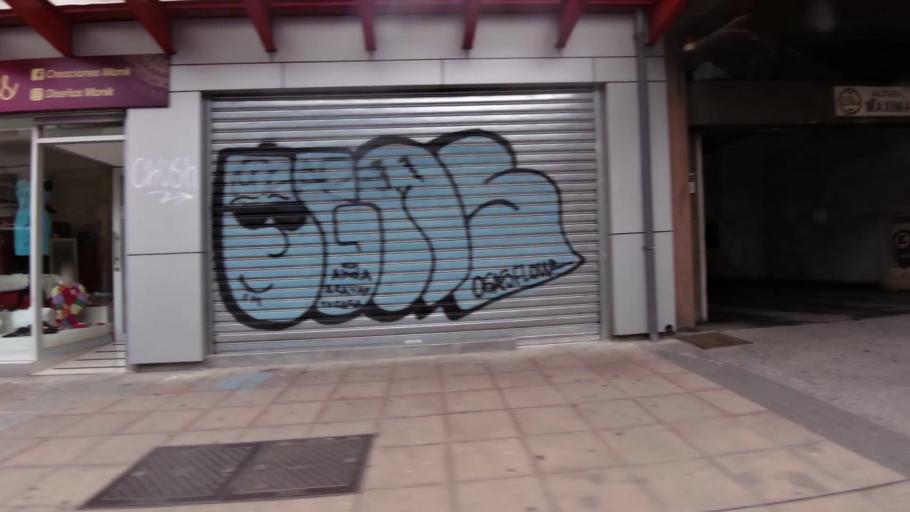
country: CL
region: Biobio
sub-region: Provincia de Concepcion
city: Concepcion
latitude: -36.8289
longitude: -73.0504
